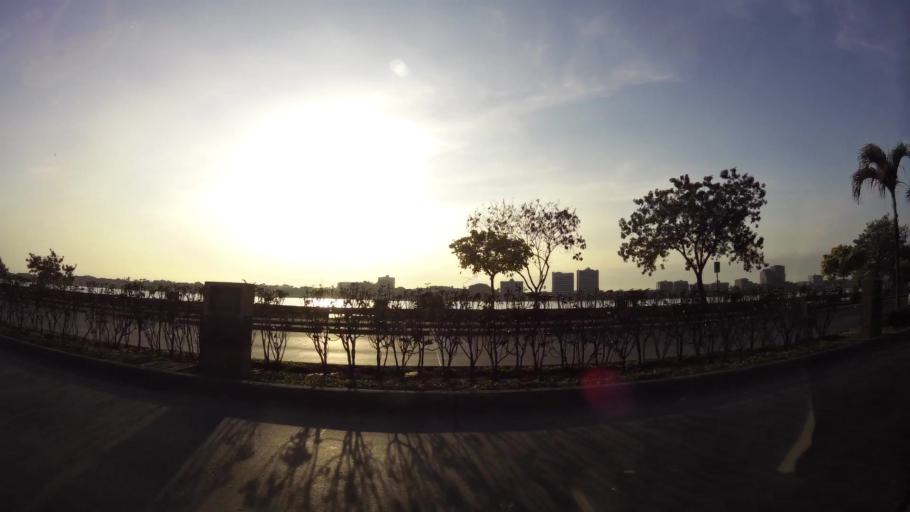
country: EC
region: Guayas
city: Eloy Alfaro
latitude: -2.1464
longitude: -79.8767
